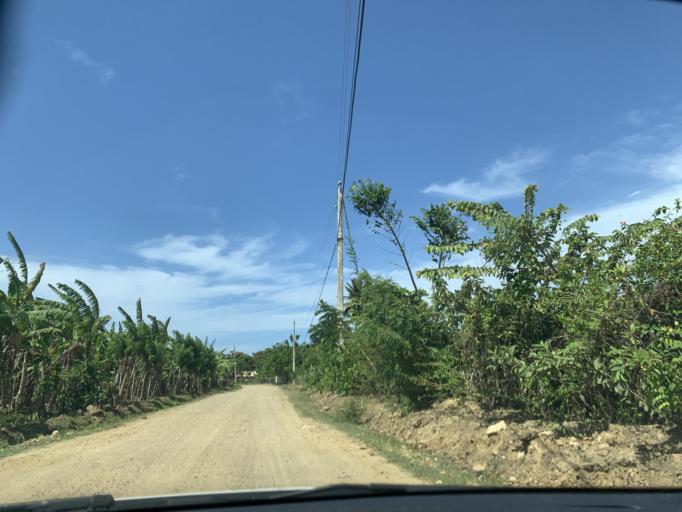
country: DO
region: Puerto Plata
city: Luperon
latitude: 19.8946
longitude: -70.8817
